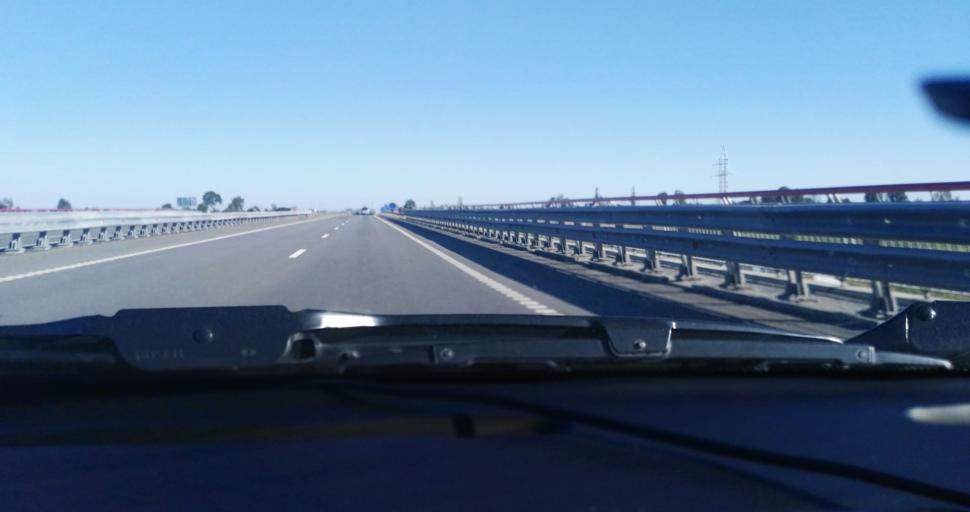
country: BY
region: Gomel
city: Buda-Kashalyova
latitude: 52.5140
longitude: 30.6295
